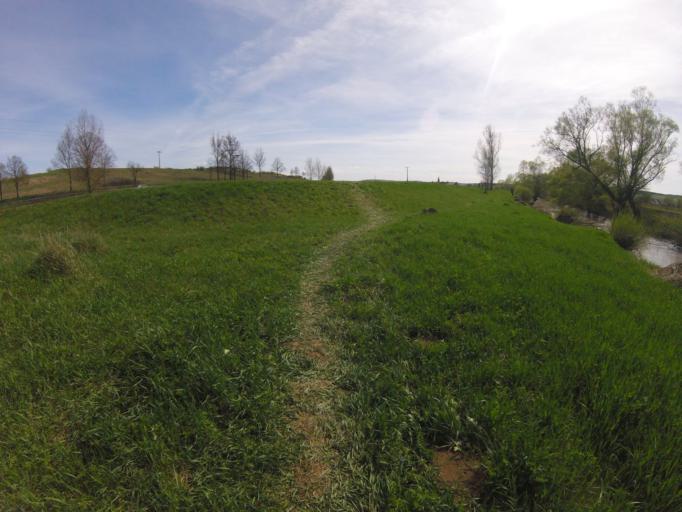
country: HU
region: Borsod-Abauj-Zemplen
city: Szendro
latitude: 48.4175
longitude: 20.7276
